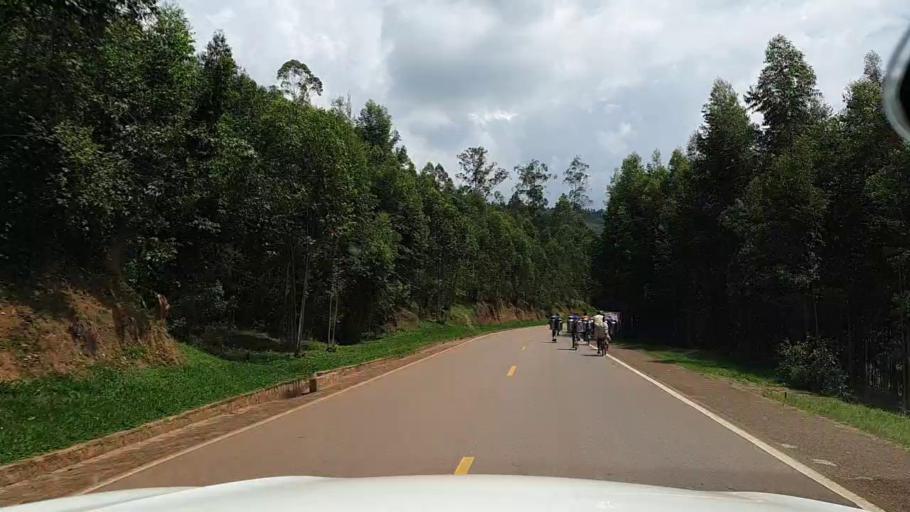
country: RW
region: Kigali
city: Kigali
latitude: -1.8163
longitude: 30.0932
